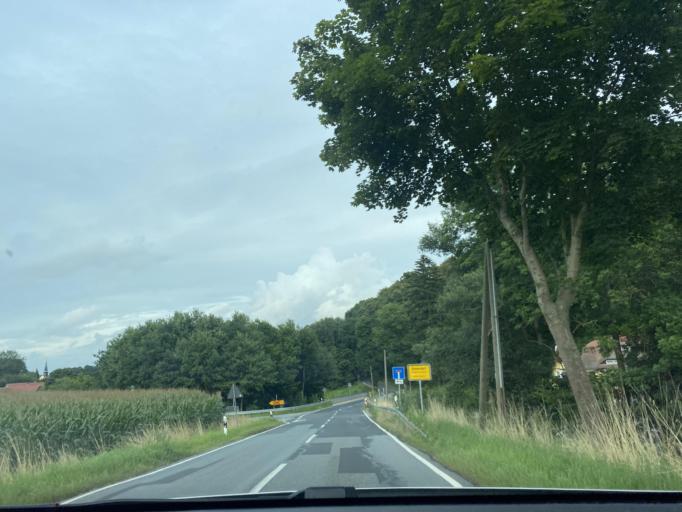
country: DE
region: Saxony
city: Grosshennersdorf
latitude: 51.0198
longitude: 14.7832
